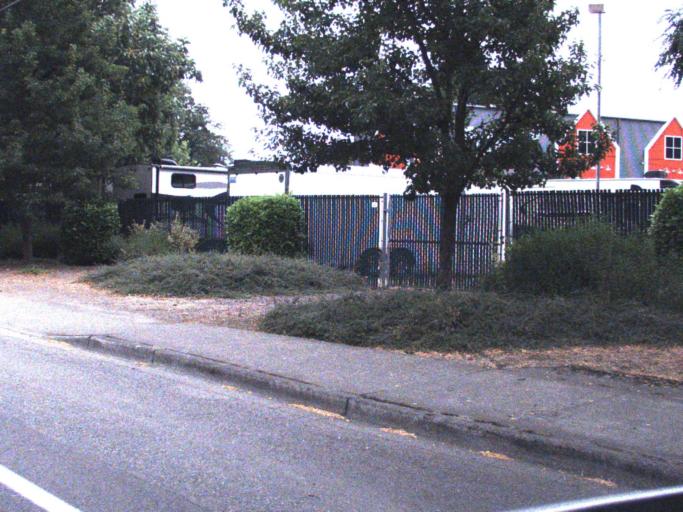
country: US
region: Washington
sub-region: King County
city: Carnation
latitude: 47.6435
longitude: -121.9153
